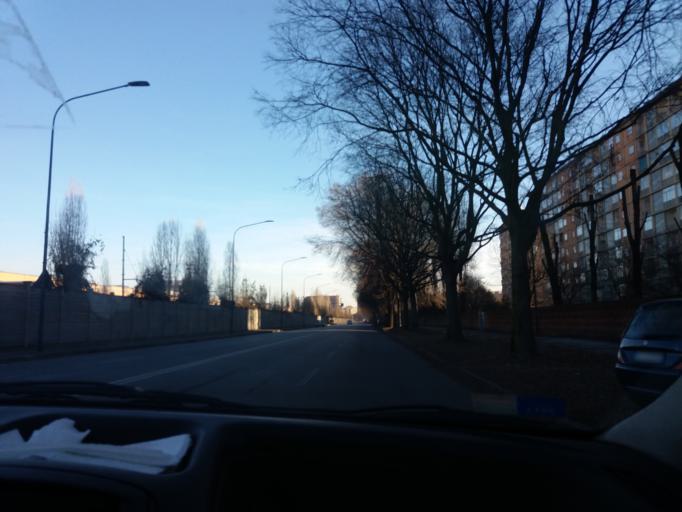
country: IT
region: Piedmont
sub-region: Provincia di Torino
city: Gerbido
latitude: 45.0227
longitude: 7.6236
